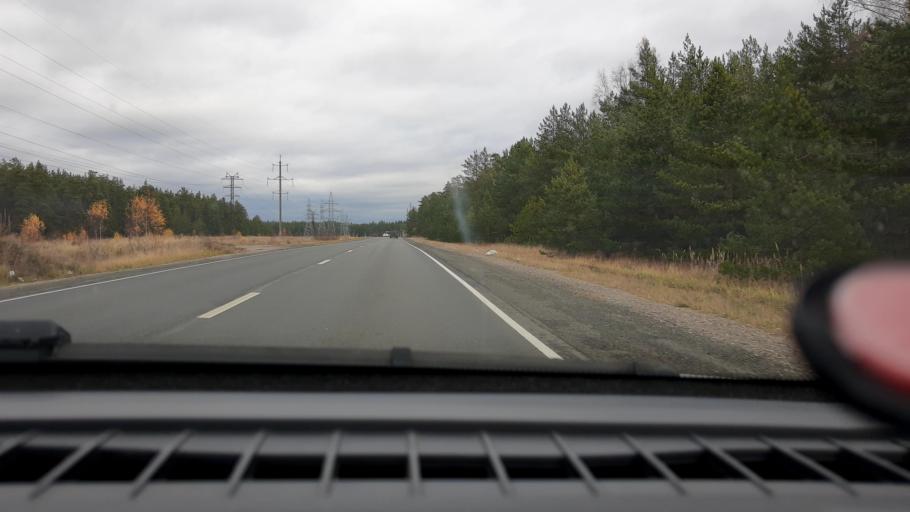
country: RU
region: Nizjnij Novgorod
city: Lukino
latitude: 56.3970
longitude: 43.6490
